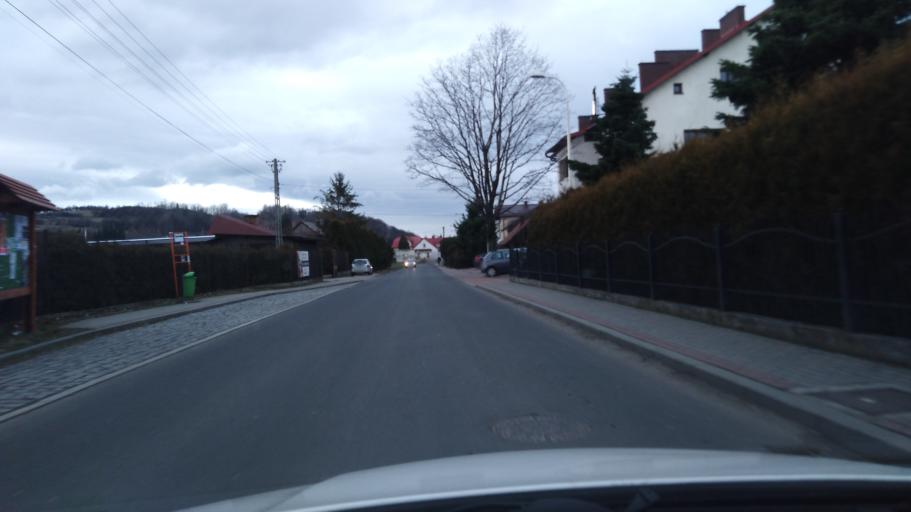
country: PL
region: Silesian Voivodeship
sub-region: Powiat zywiecki
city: Trzebinia
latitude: 49.6716
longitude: 19.2153
